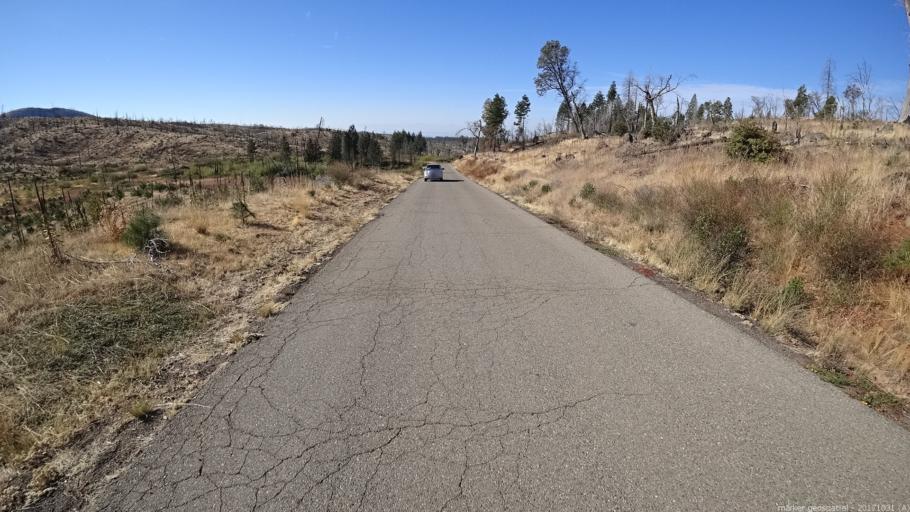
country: US
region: California
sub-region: Shasta County
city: Shingletown
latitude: 40.4567
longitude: -121.7854
